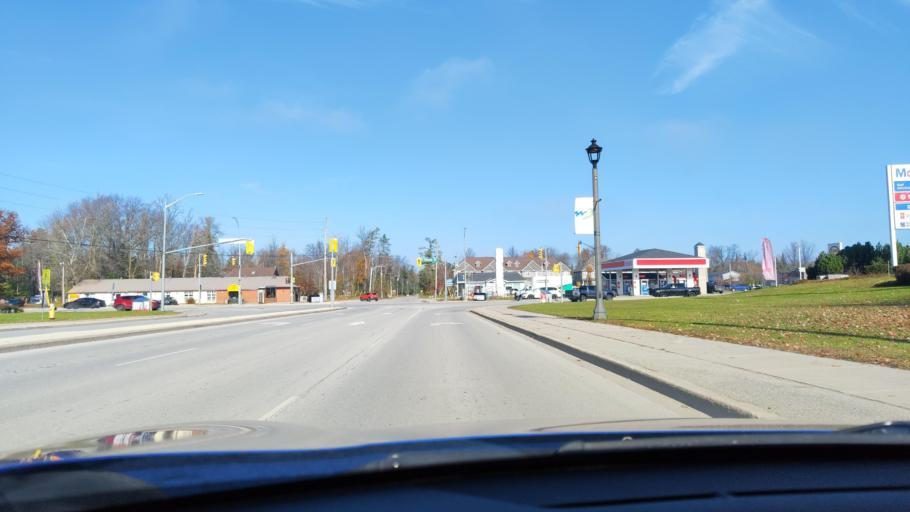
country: CA
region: Ontario
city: Wasaga Beach
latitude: 44.4734
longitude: -80.0760
